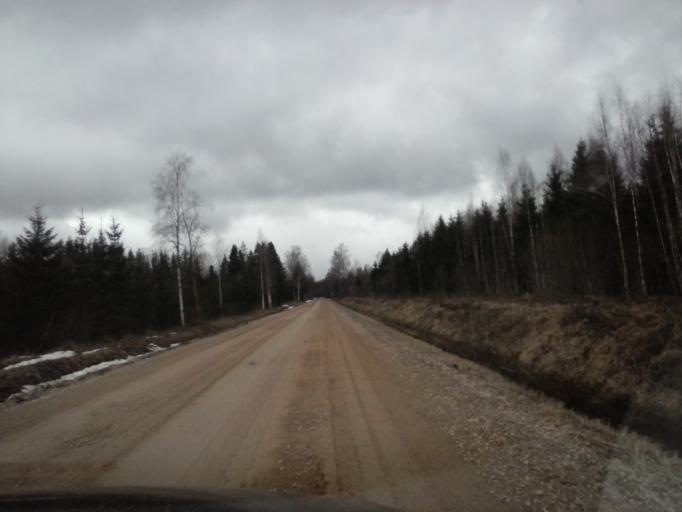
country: EE
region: Jogevamaa
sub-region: Mustvee linn
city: Mustvee
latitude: 59.0825
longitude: 26.8431
